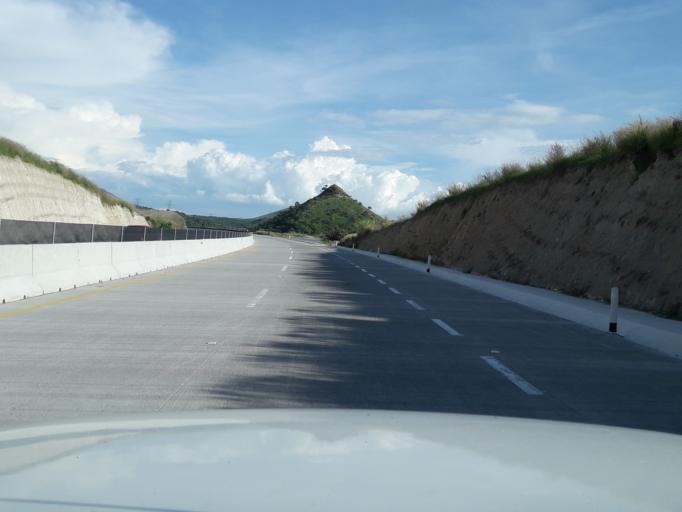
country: MX
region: Jalisco
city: Tala
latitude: 20.6027
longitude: -103.6773
